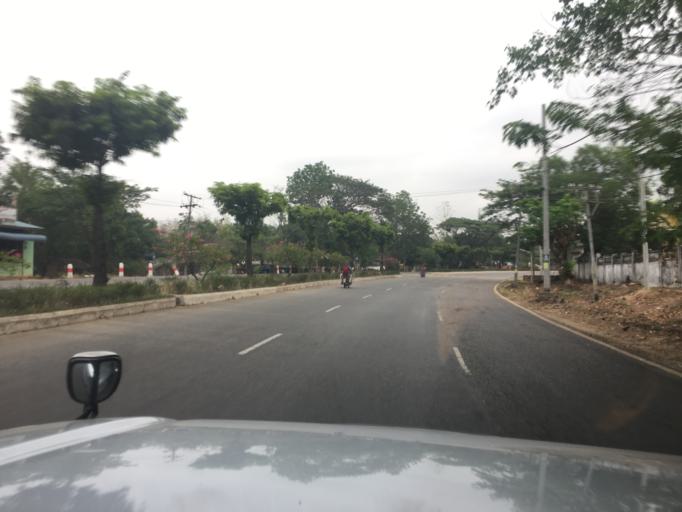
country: MM
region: Bago
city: Thanatpin
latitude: 17.1980
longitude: 96.4010
